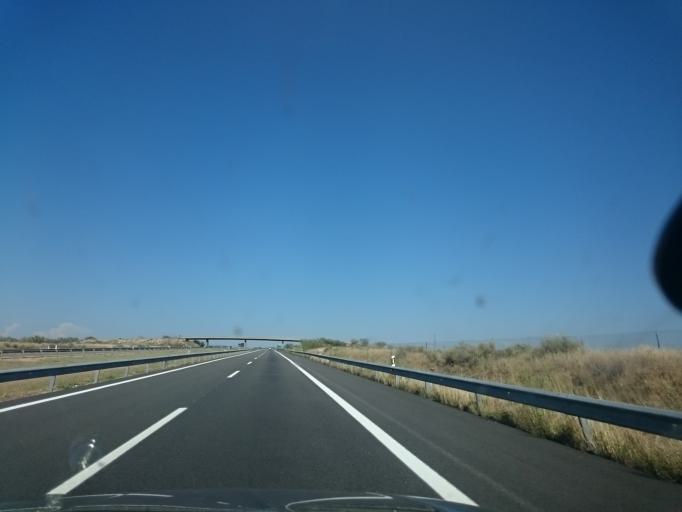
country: ES
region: Aragon
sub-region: Provincia de Zaragoza
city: Mequinensa / Mequinenza
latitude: 41.4681
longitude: 0.2496
